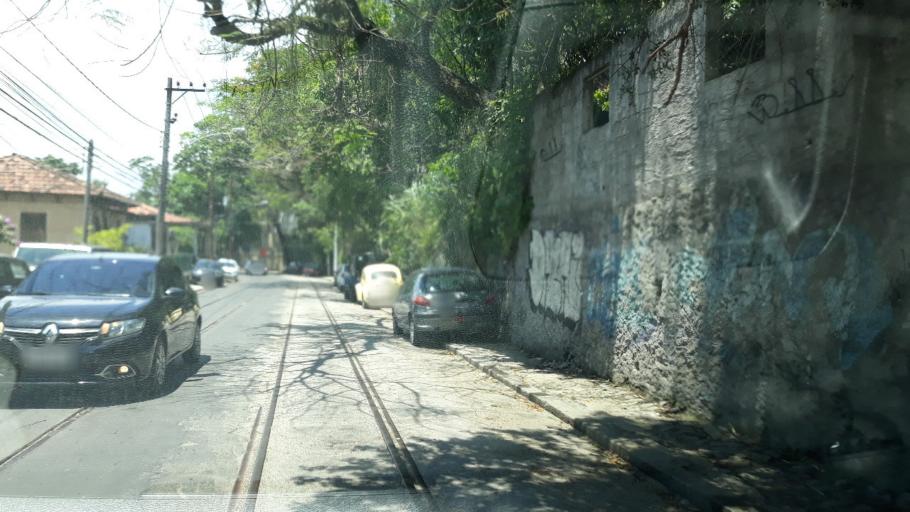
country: BR
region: Rio de Janeiro
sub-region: Rio De Janeiro
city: Rio de Janeiro
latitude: -22.9340
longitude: -43.1990
